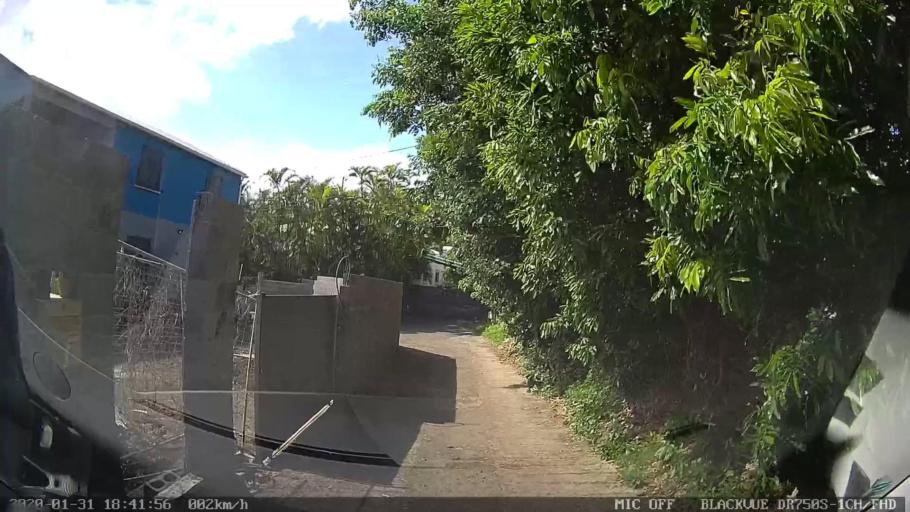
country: RE
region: Reunion
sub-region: Reunion
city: Sainte-Marie
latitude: -20.9161
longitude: 55.5303
